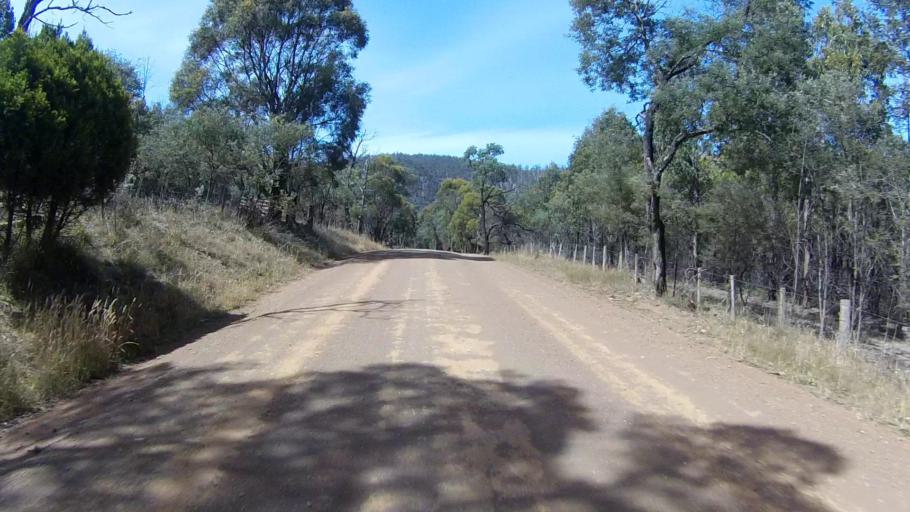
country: AU
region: Tasmania
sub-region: Sorell
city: Sorell
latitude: -42.6336
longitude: 147.7241
